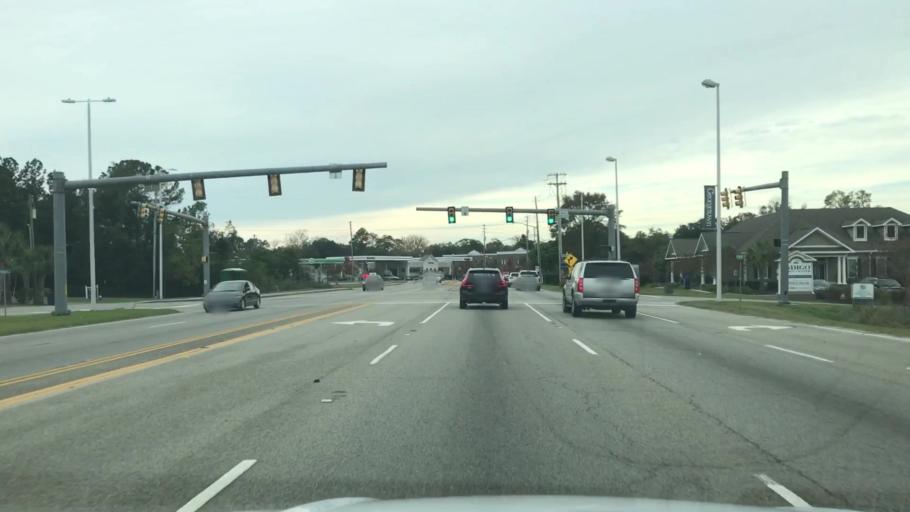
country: US
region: South Carolina
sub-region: Georgetown County
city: Georgetown
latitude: 33.3675
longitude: -79.2722
